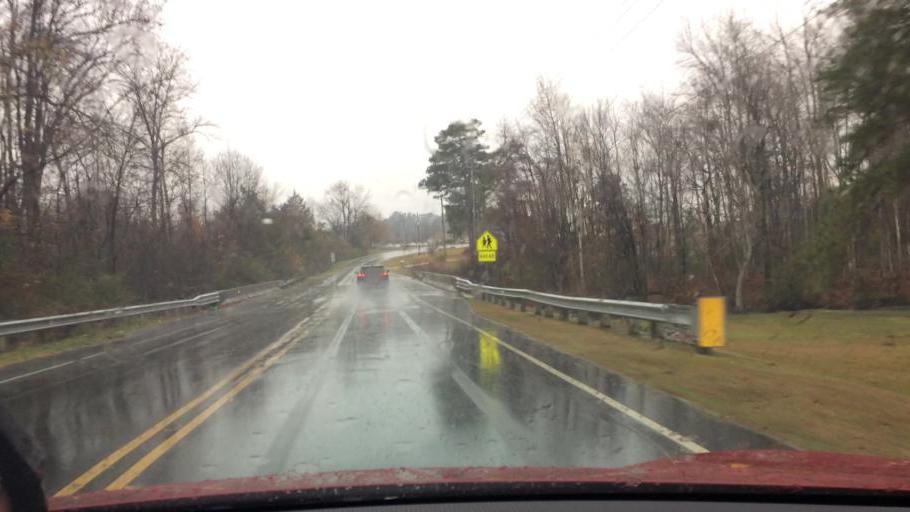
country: US
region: North Carolina
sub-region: Wayne County
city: Goldsboro
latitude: 35.4131
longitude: -77.9324
